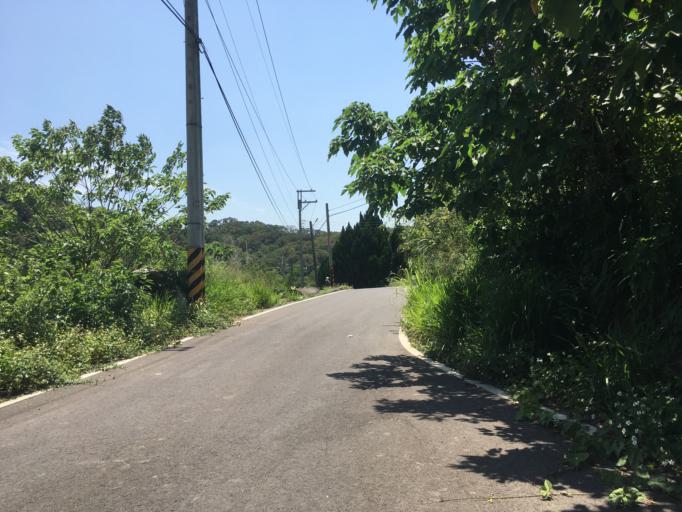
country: TW
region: Taiwan
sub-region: Hsinchu
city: Hsinchu
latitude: 24.7313
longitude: 120.9855
